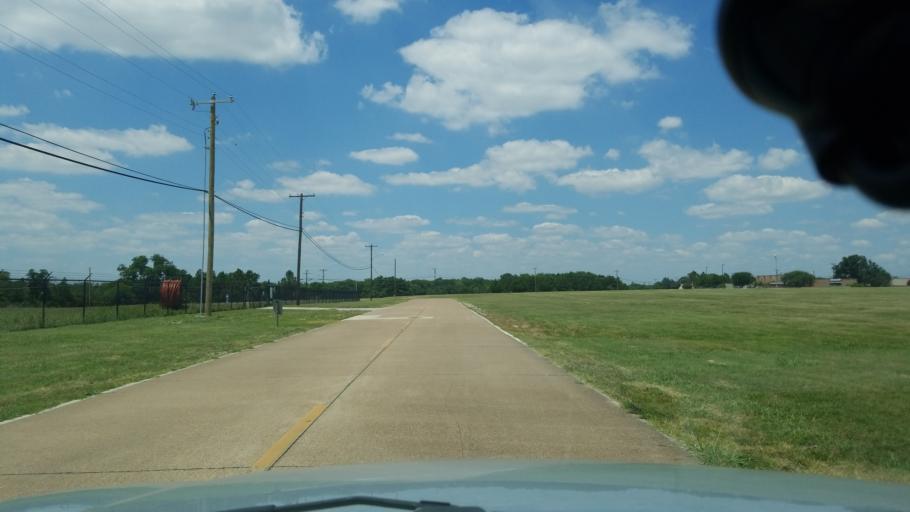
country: US
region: Texas
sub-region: Dallas County
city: Duncanville
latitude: 32.6822
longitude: -96.8590
